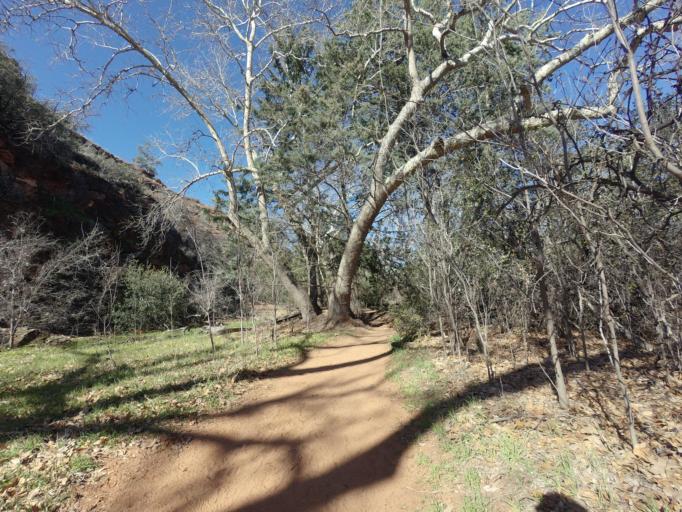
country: US
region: Arizona
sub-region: Yavapai County
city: West Sedona
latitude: 34.8228
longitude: -111.8018
